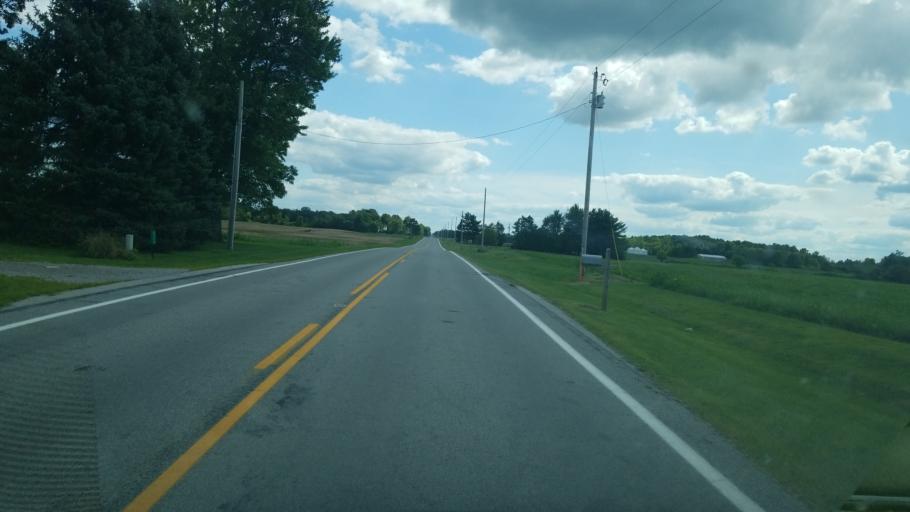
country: US
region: Ohio
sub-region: Allen County
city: Lima
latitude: 40.6797
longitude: -83.9758
